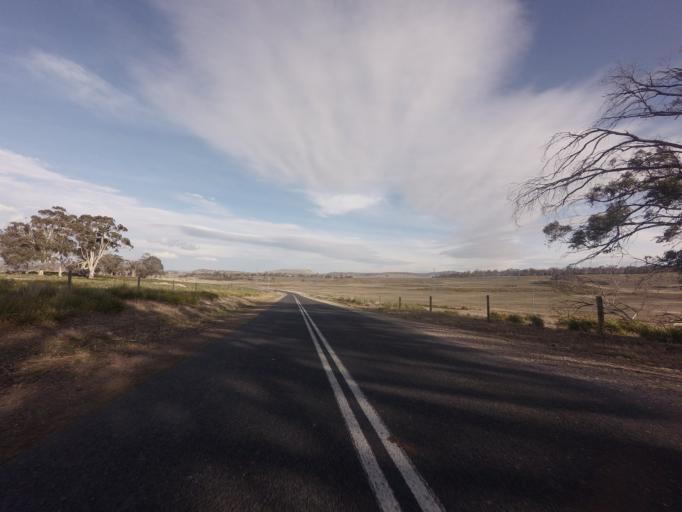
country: AU
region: Tasmania
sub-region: Derwent Valley
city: New Norfolk
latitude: -42.2459
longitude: 146.9256
